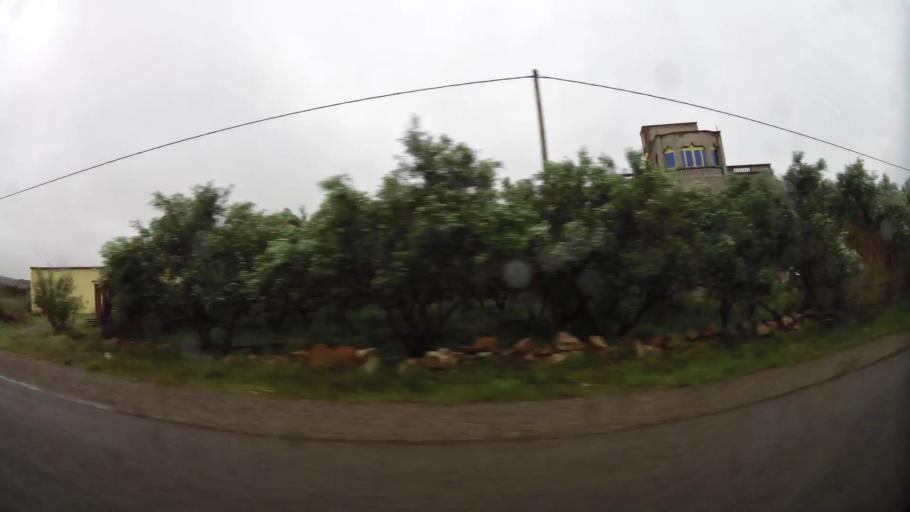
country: MA
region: Oriental
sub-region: Nador
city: Boudinar
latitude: 35.1168
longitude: -3.5766
